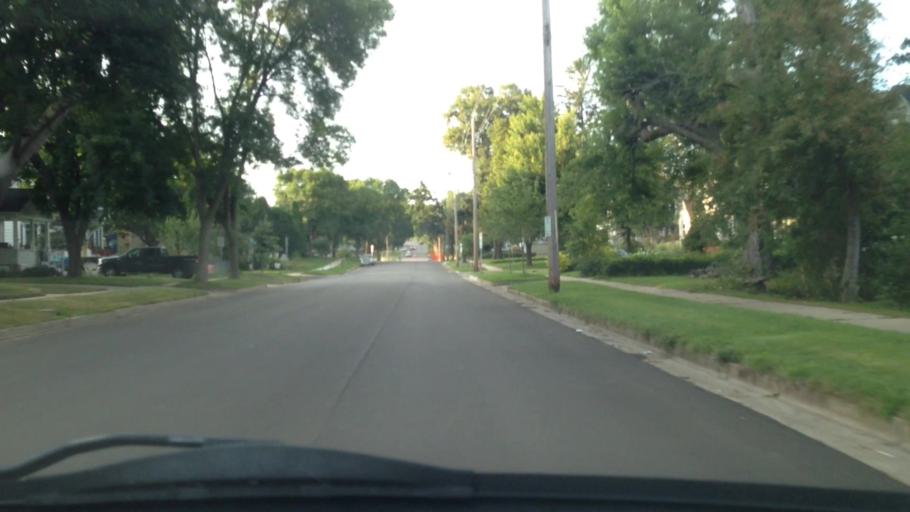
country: US
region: Minnesota
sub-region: Olmsted County
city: Rochester
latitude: 44.0140
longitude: -92.4714
